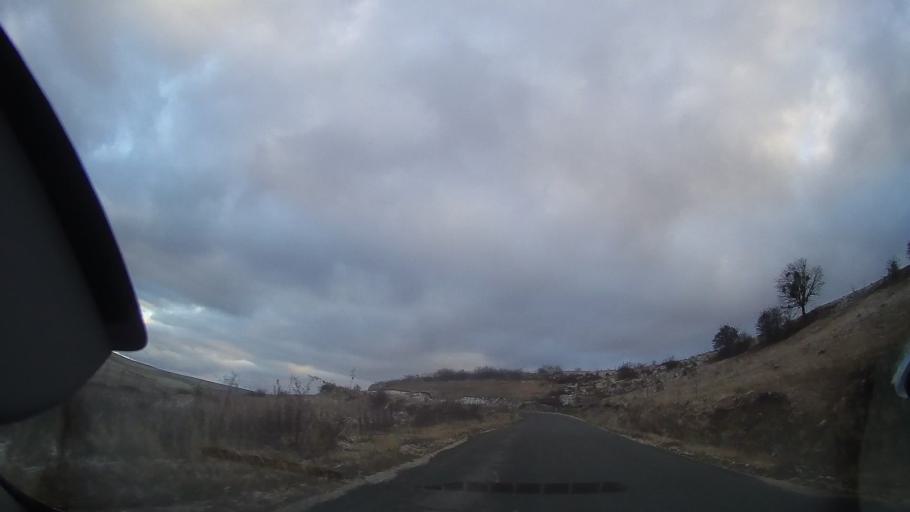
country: RO
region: Cluj
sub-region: Comuna Manastireni
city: Manastireni
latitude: 46.7817
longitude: 23.0517
